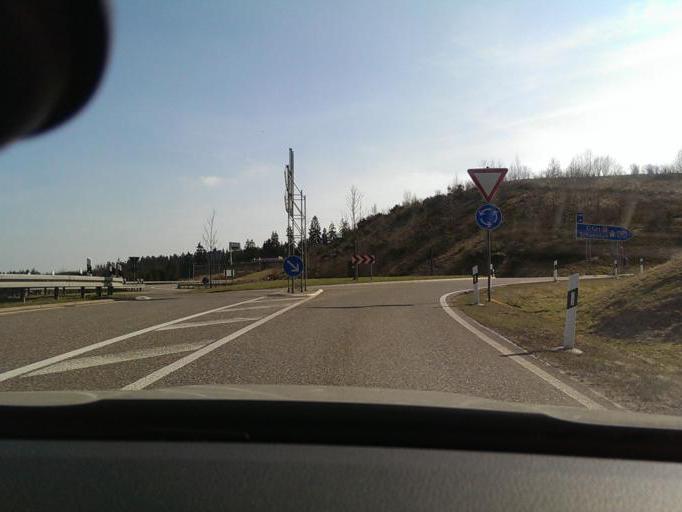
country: DE
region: Thuringia
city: Suhl
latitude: 50.5774
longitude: 10.7248
